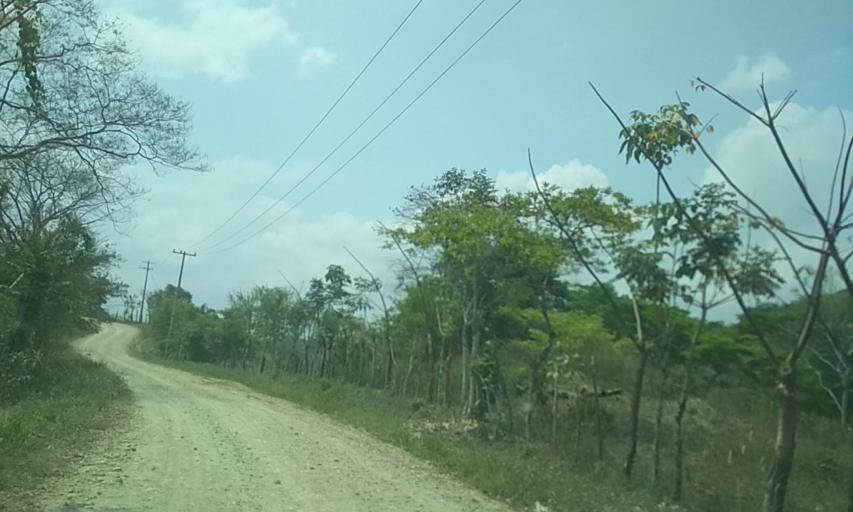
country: MX
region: Tabasco
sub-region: Huimanguillo
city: Francisco Rueda
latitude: 17.6396
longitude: -93.8242
